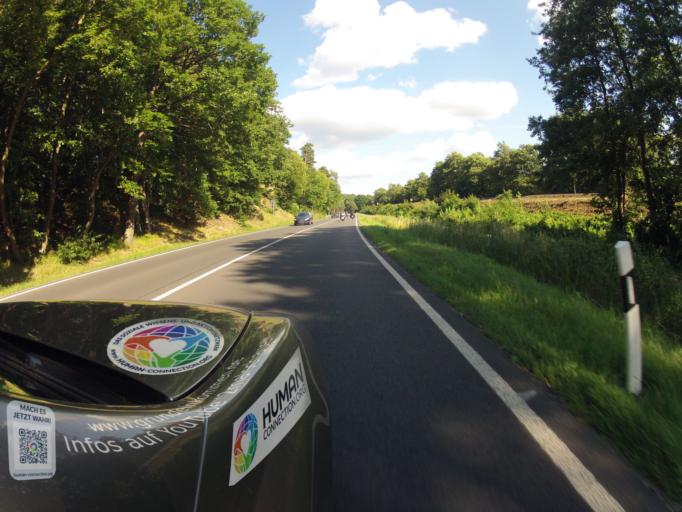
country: DE
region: Mecklenburg-Vorpommern
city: Seebad Bansin
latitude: 53.9790
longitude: 14.0984
